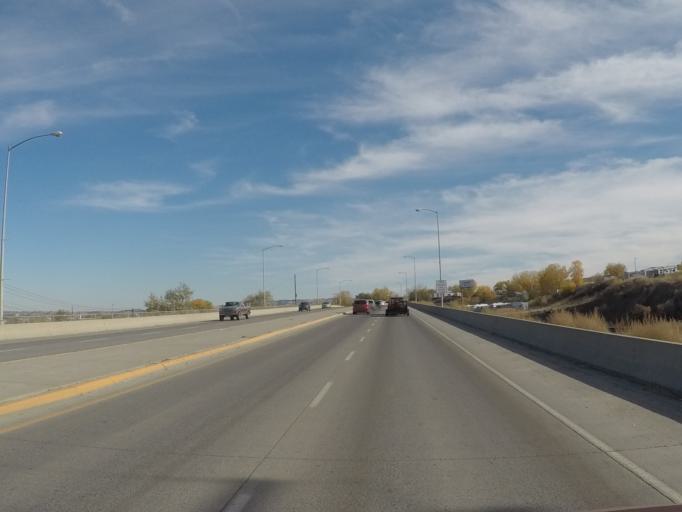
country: US
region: Montana
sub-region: Yellowstone County
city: Billings
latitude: 45.7963
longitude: -108.4685
